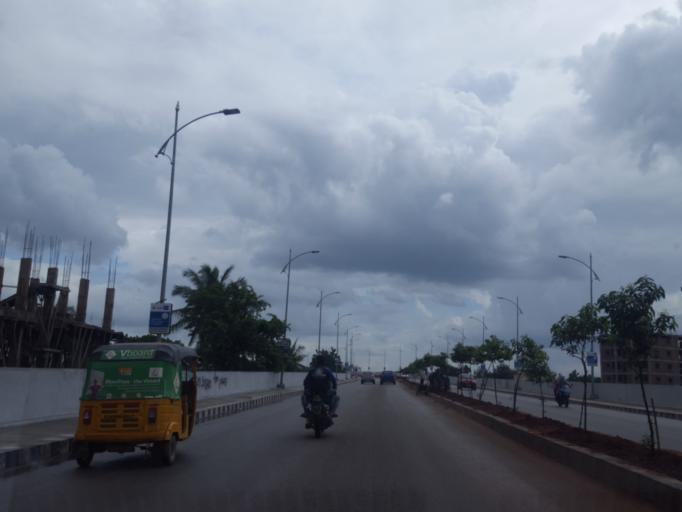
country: IN
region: Telangana
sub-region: Medak
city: Serilingampalle
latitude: 17.4846
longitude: 78.3123
